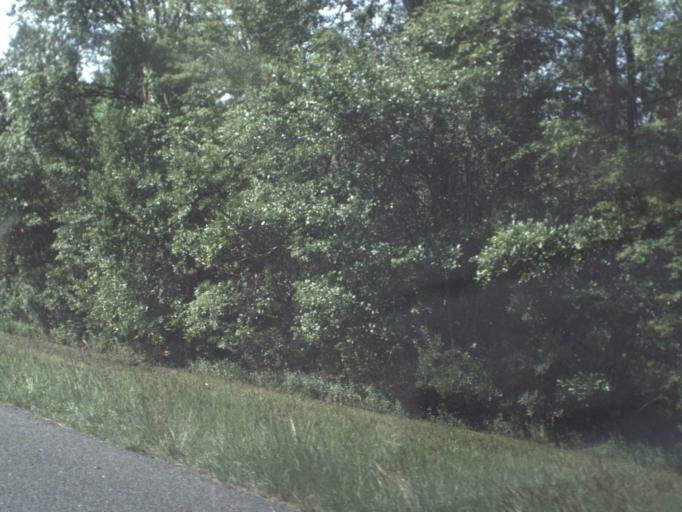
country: US
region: Florida
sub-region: Nassau County
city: Hilliard
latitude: 30.7438
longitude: -81.9549
